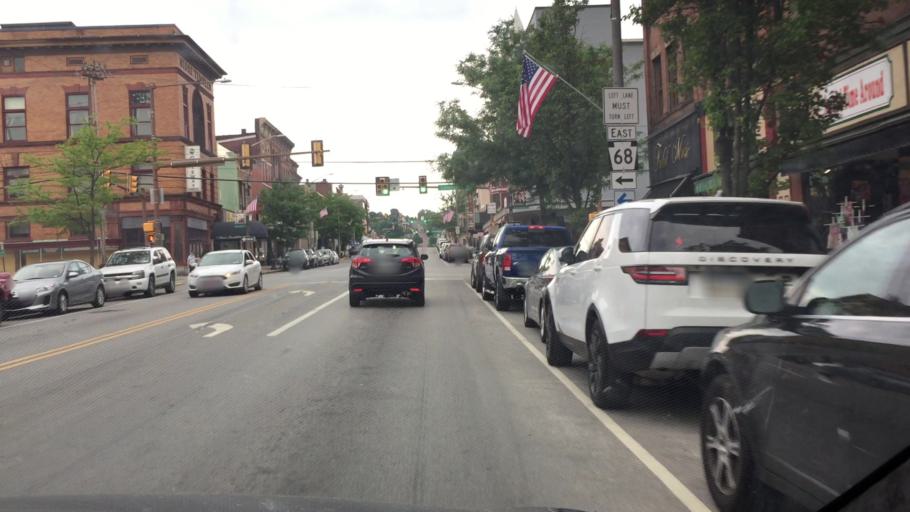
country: US
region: Pennsylvania
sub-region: Butler County
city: Butler
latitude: 40.8603
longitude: -79.8953
